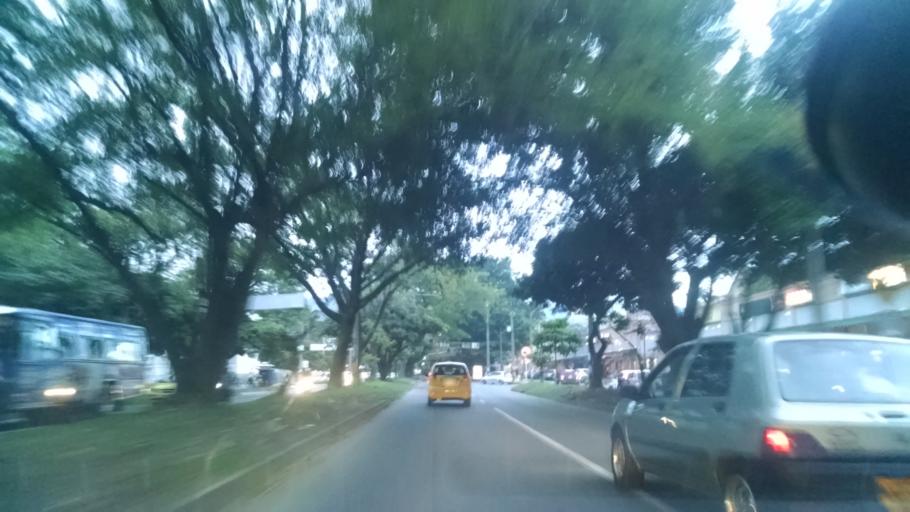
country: CO
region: Antioquia
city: Itagui
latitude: 6.2154
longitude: -75.5973
